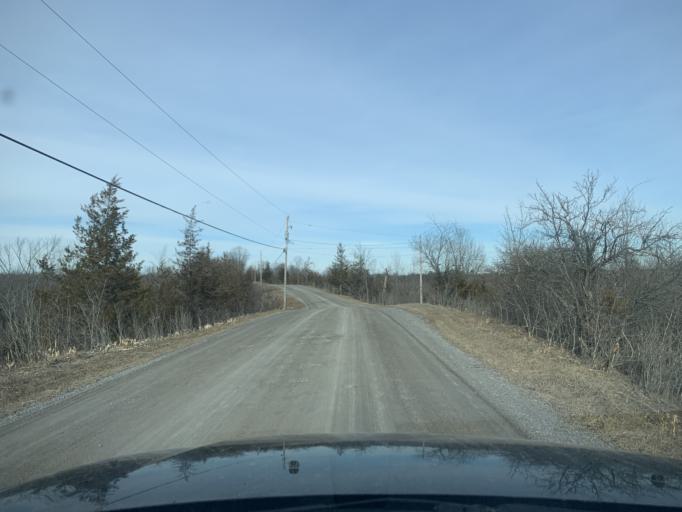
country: CA
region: Ontario
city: Deseronto
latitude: 44.4067
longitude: -77.1196
